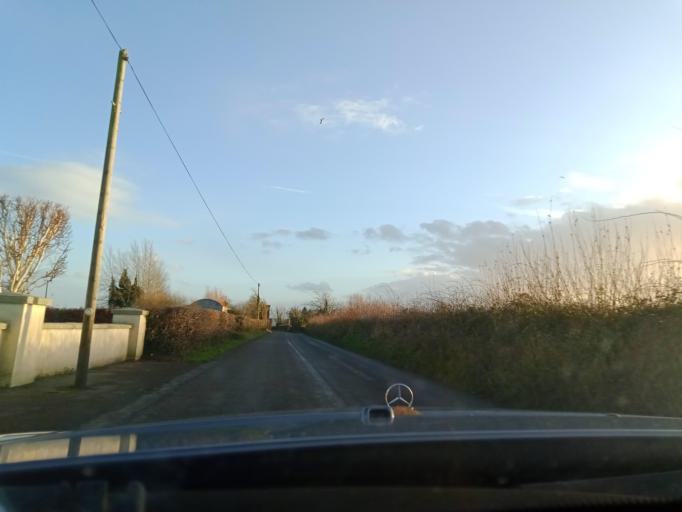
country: IE
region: Leinster
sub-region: Kilkenny
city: Callan
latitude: 52.5012
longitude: -7.3417
